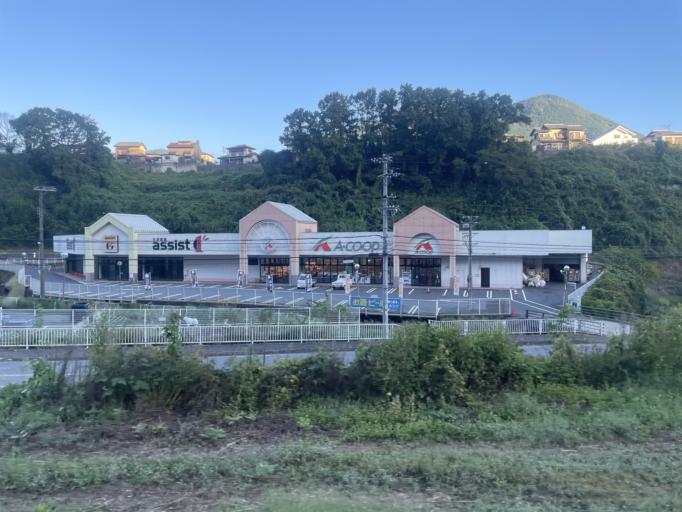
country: JP
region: Nara
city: Haibara-akanedai
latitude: 34.5435
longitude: 135.9768
